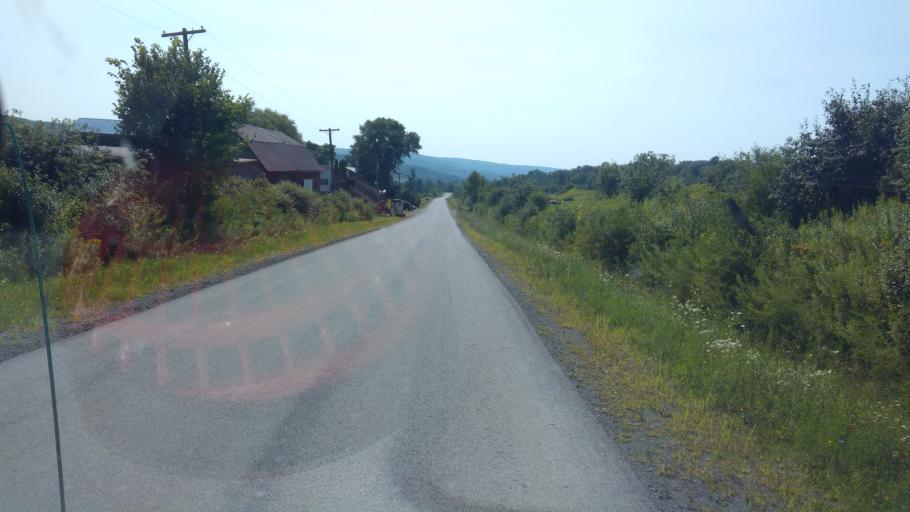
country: US
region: New York
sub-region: Allegany County
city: Belmont
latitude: 42.3401
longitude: -78.0412
